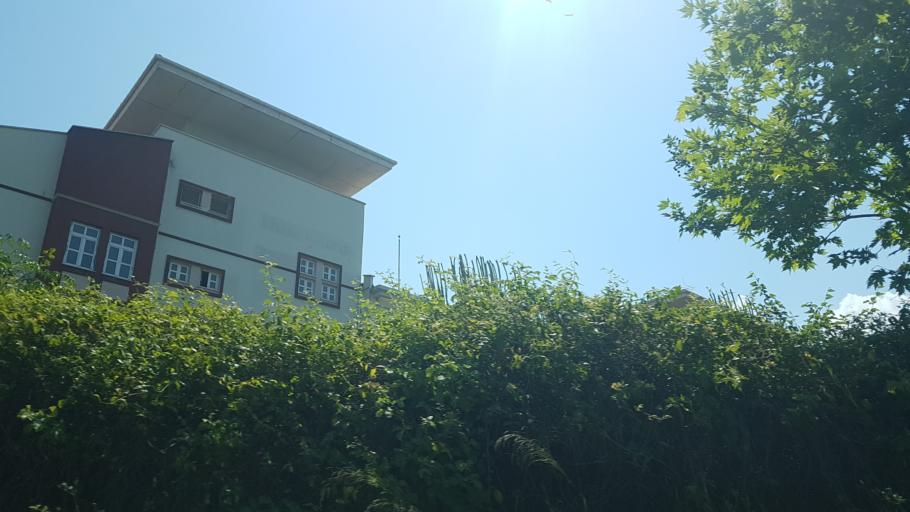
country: TR
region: Adana
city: Adana
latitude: 37.0292
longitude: 35.3580
